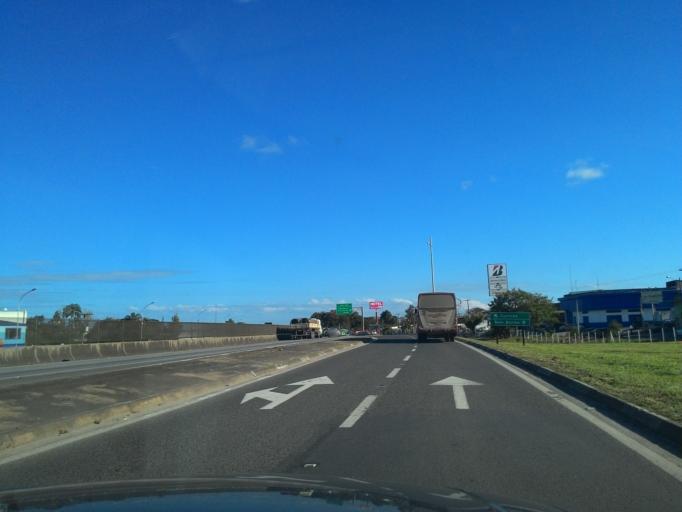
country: BR
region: Sao Paulo
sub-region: Registro
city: Registro
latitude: -24.5016
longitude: -47.8466
